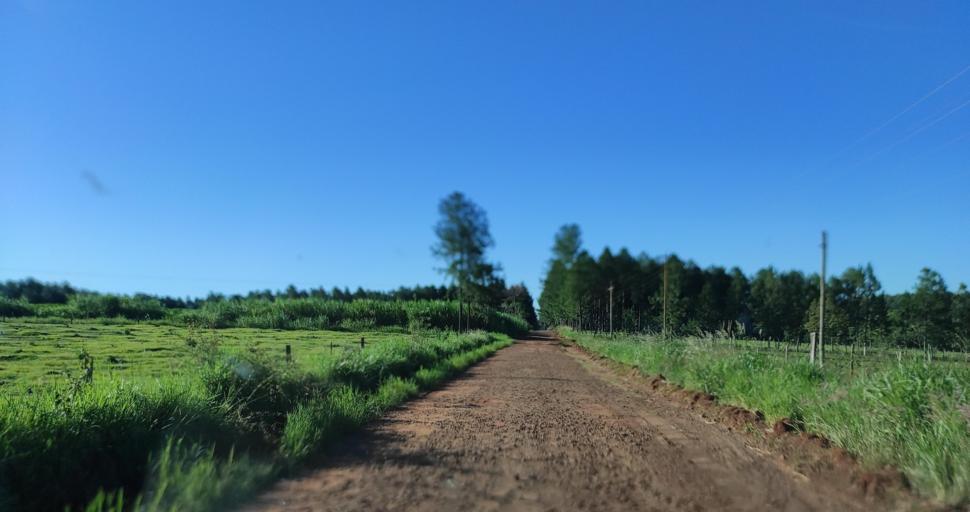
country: AR
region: Misiones
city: Puerto Rico
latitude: -26.8445
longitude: -55.0028
